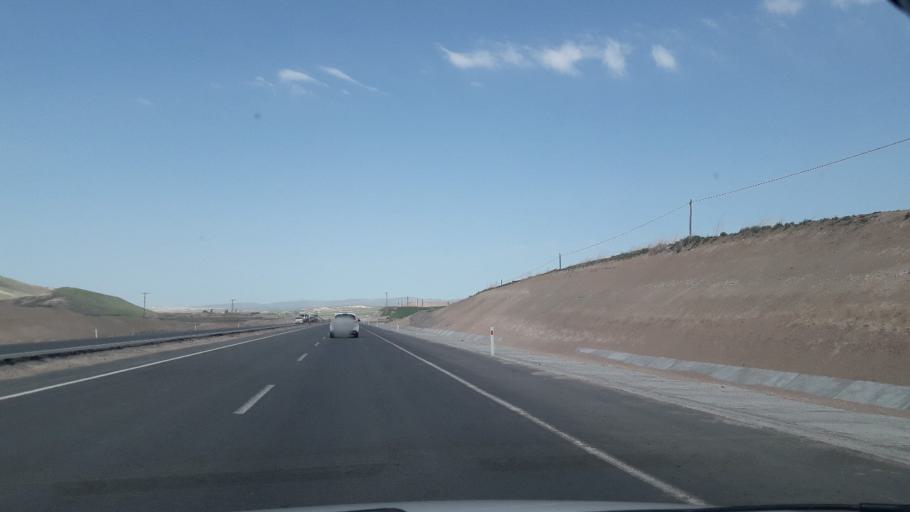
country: TR
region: Sivas
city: Deliktas
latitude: 39.2057
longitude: 37.2134
